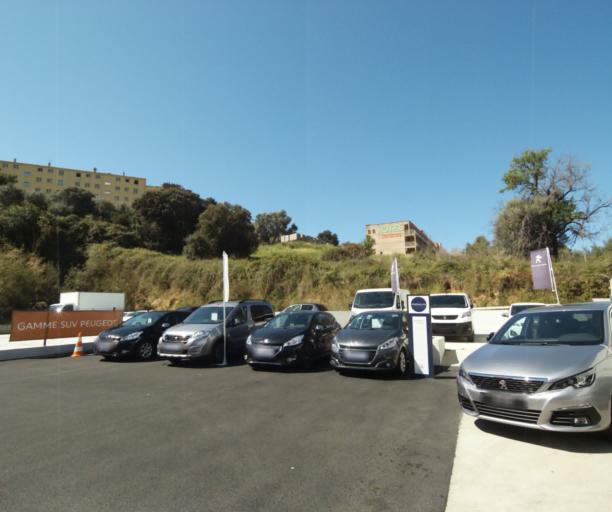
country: FR
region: Corsica
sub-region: Departement de la Corse-du-Sud
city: Propriano
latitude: 41.6764
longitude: 8.9094
